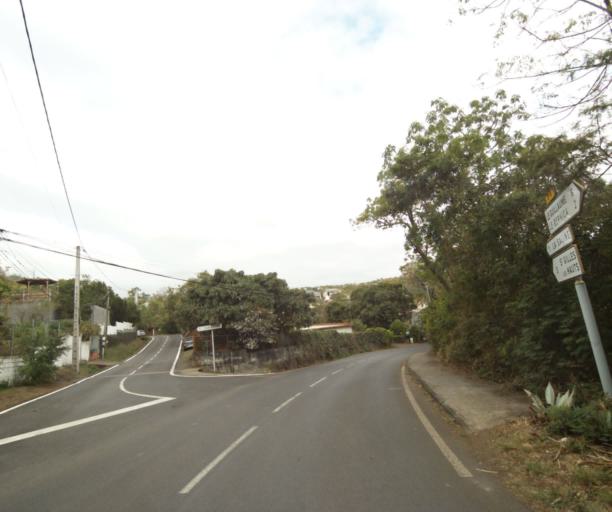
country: RE
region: Reunion
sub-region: Reunion
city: Saint-Paul
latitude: -21.0542
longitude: 55.2830
